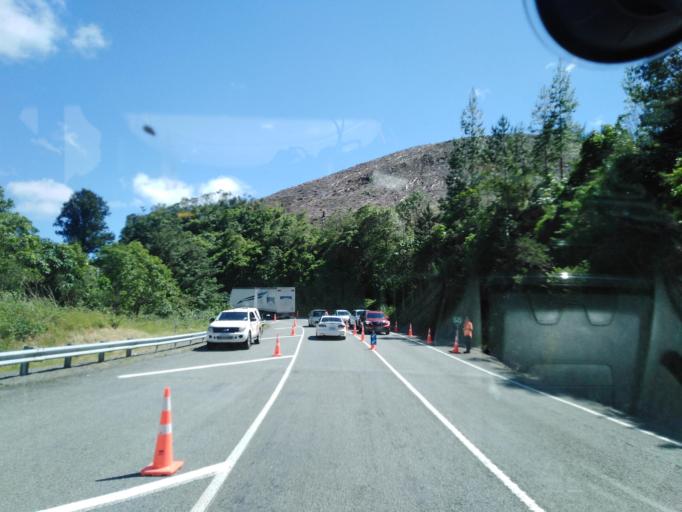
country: NZ
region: Nelson
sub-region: Nelson City
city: Nelson
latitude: -41.2032
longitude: 173.5632
